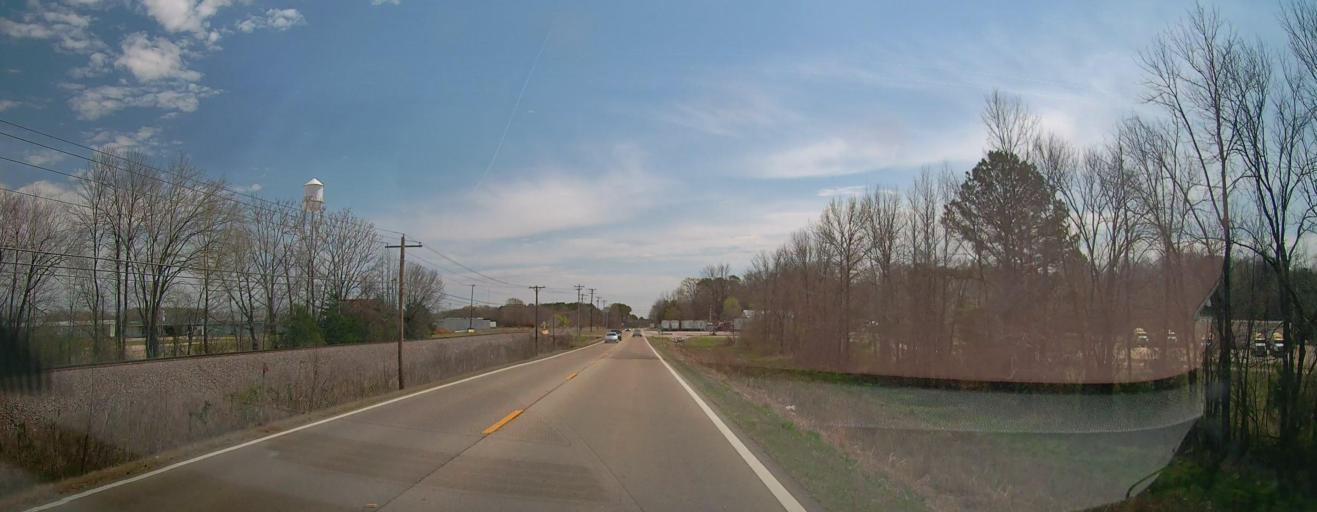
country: US
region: Mississippi
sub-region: Union County
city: New Albany
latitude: 34.5172
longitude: -89.0485
